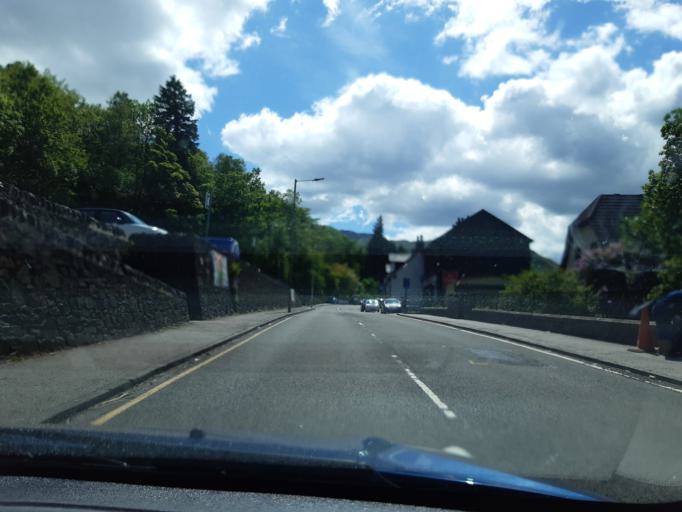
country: GB
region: Scotland
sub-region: Argyll and Bute
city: Garelochhead
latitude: 56.2043
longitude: -4.7435
